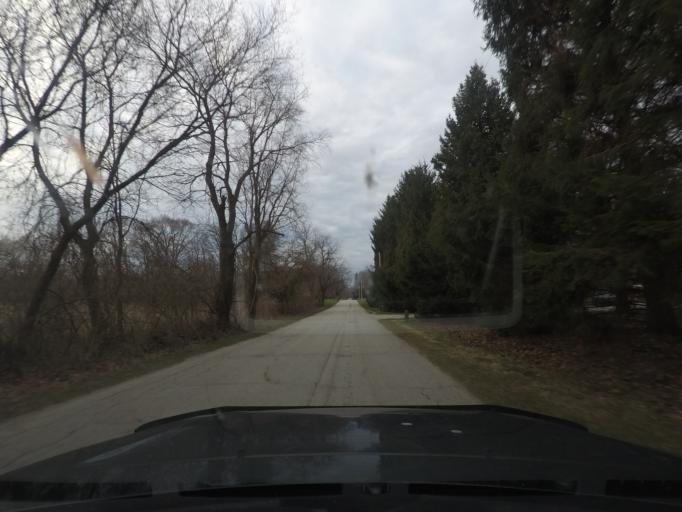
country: US
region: Indiana
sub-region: LaPorte County
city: Westville
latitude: 41.5239
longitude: -86.7988
